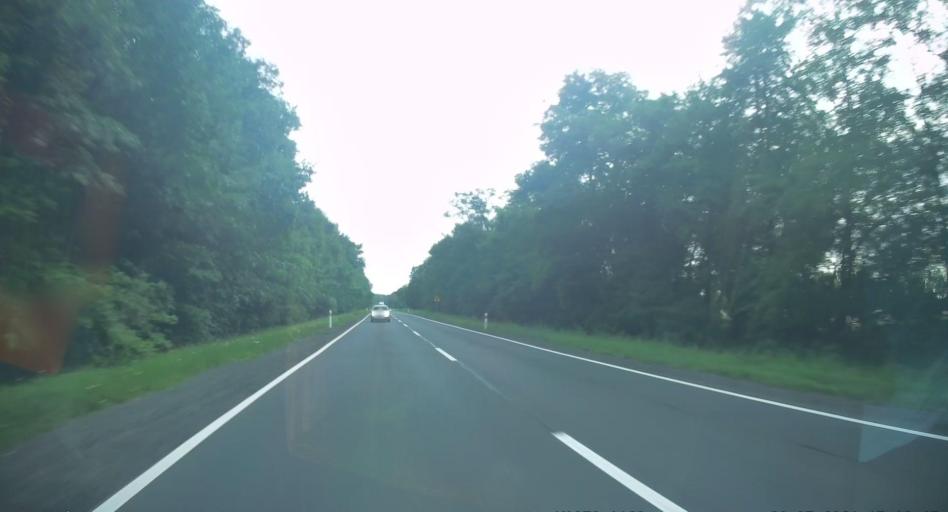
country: PL
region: Lodz Voivodeship
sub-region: Powiat radomszczanski
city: Plawno
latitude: 50.9645
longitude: 19.4058
